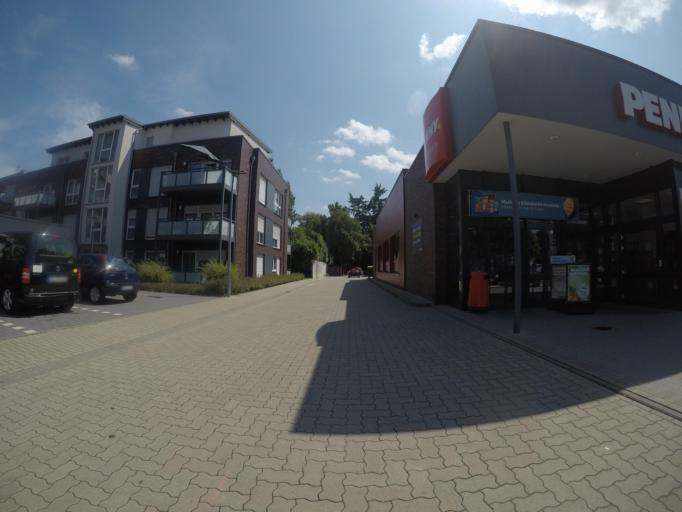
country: DE
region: North Rhine-Westphalia
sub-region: Regierungsbezirk Dusseldorf
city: Kleve
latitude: 51.7753
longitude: 6.1203
